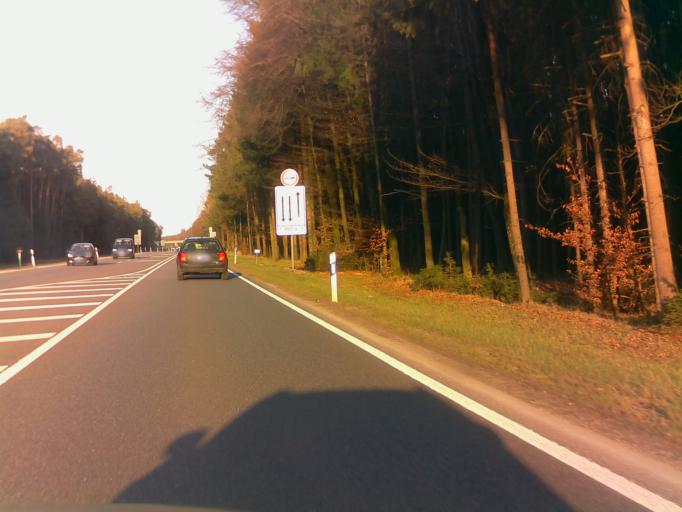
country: DE
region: Bavaria
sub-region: Upper Bavaria
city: Munchsmunster
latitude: 48.7502
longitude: 11.6688
